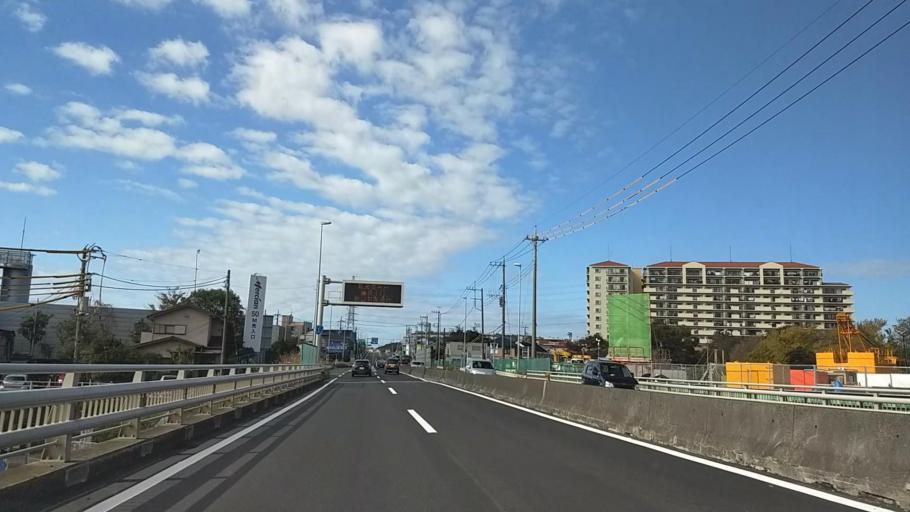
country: JP
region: Kanagawa
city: Fujisawa
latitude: 35.3490
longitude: 139.4642
